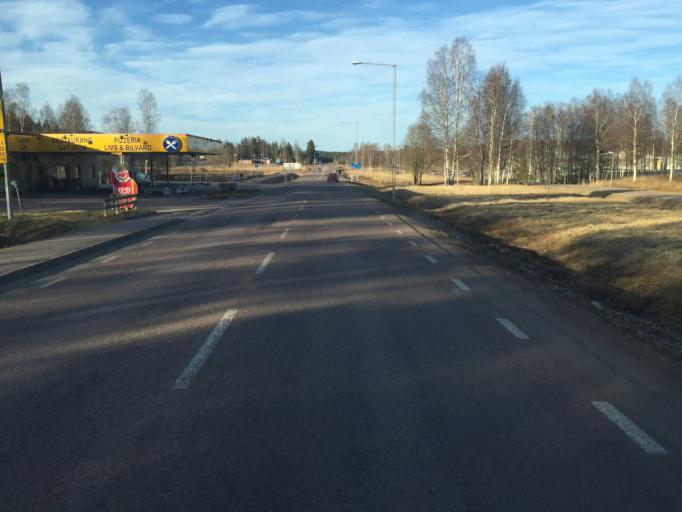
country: SE
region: Dalarna
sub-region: Gagnefs Kommun
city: Mockfjard
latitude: 60.5079
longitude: 14.9617
